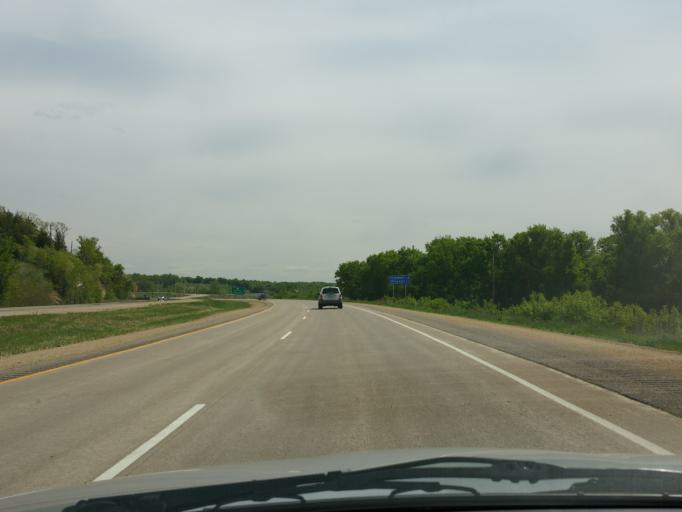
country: US
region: Wisconsin
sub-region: Pierce County
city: River Falls
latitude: 44.9036
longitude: -92.6566
